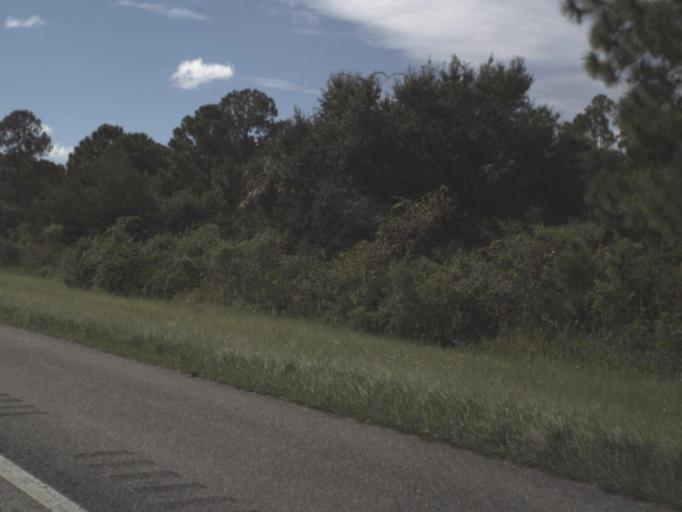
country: US
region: Florida
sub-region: Charlotte County
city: Port Charlotte
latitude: 27.0365
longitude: -82.0595
